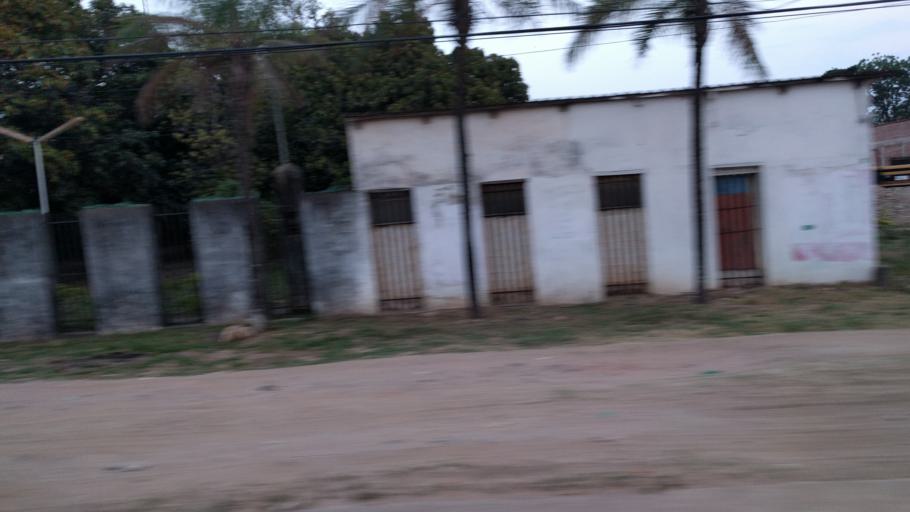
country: BO
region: Santa Cruz
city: Santa Rita
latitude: -17.8920
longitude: -63.3228
